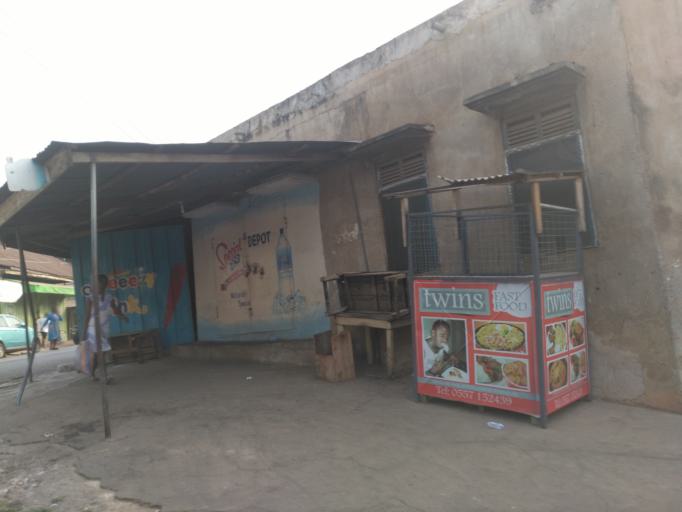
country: GH
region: Ashanti
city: Kumasi
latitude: 6.6909
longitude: -1.6133
